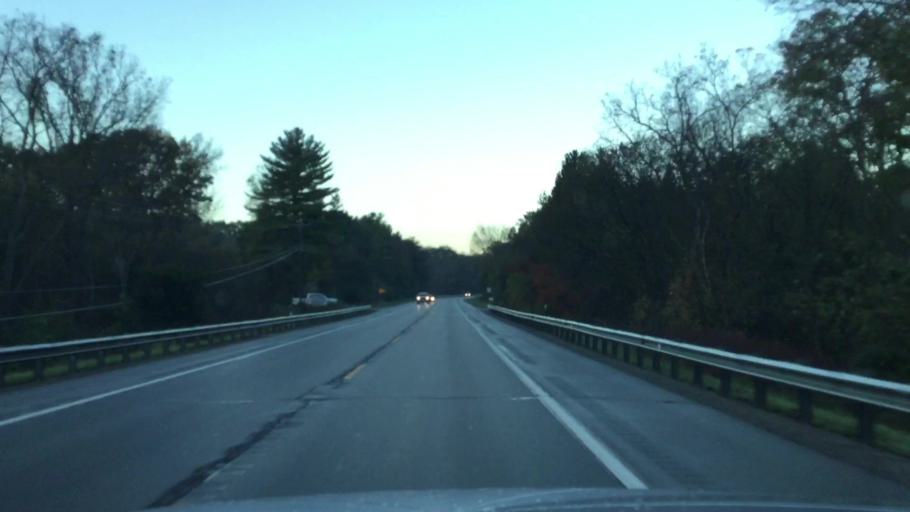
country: US
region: Michigan
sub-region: Livingston County
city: Howell
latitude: 42.6257
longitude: -83.8870
